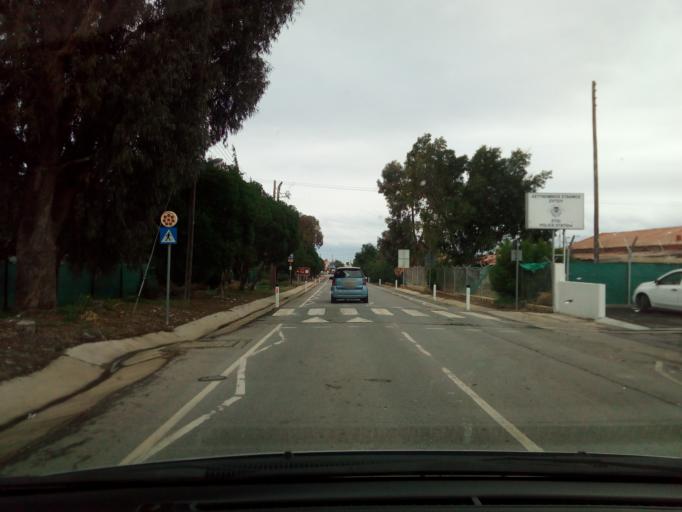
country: CY
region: Larnaka
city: Kofinou
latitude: 34.7324
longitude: 33.3353
